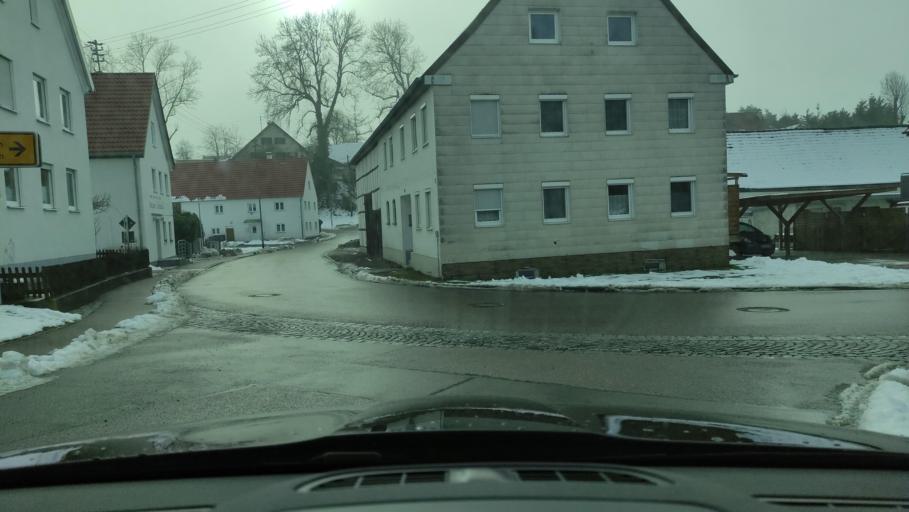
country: DE
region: Bavaria
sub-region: Swabia
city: Deisenhausen
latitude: 48.2819
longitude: 10.3307
